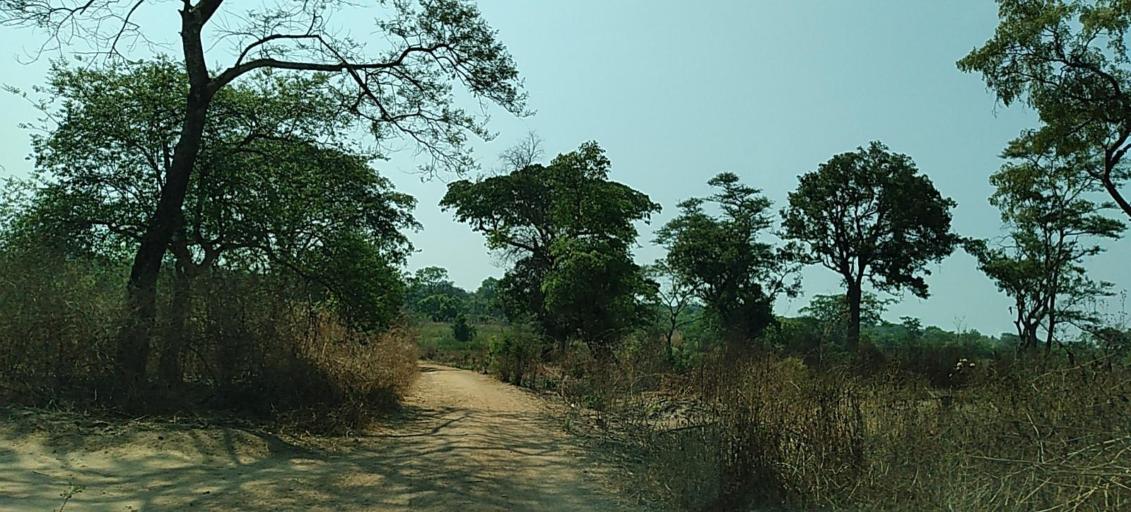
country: ZM
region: Copperbelt
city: Luanshya
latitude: -13.2804
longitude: 28.3123
